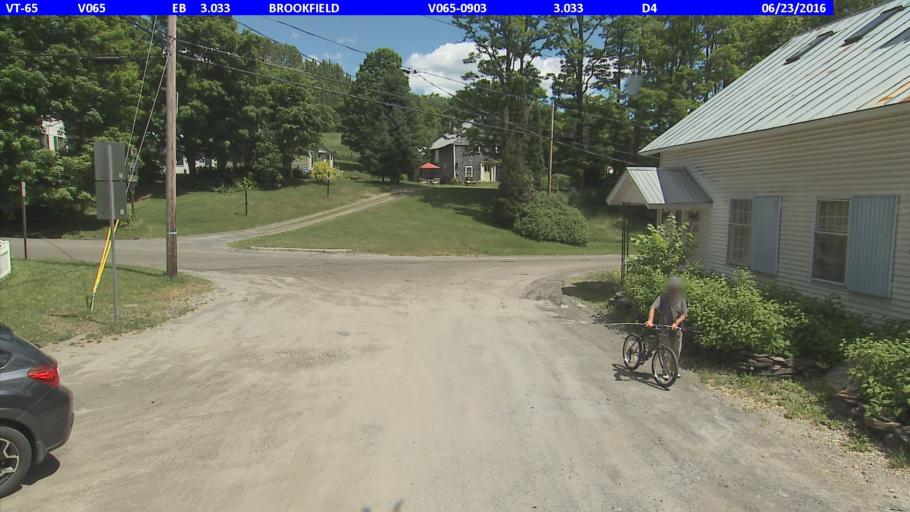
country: US
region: Vermont
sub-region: Orange County
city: Williamstown
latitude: 44.0423
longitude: -72.6038
